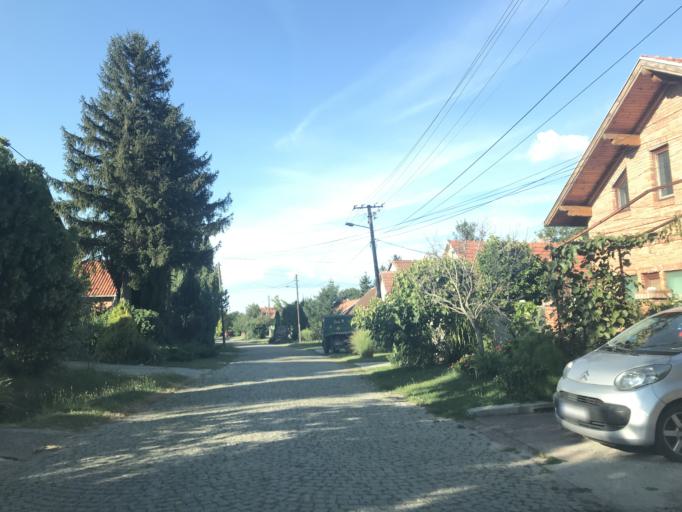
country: RS
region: Autonomna Pokrajina Vojvodina
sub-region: Juznobacki Okrug
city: Novi Sad
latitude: 45.2095
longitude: 19.8018
